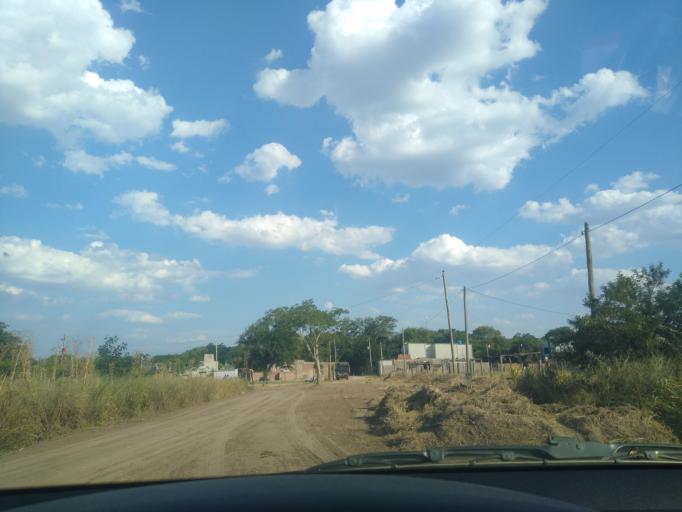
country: AR
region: Chaco
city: Resistencia
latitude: -27.4177
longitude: -58.9449
